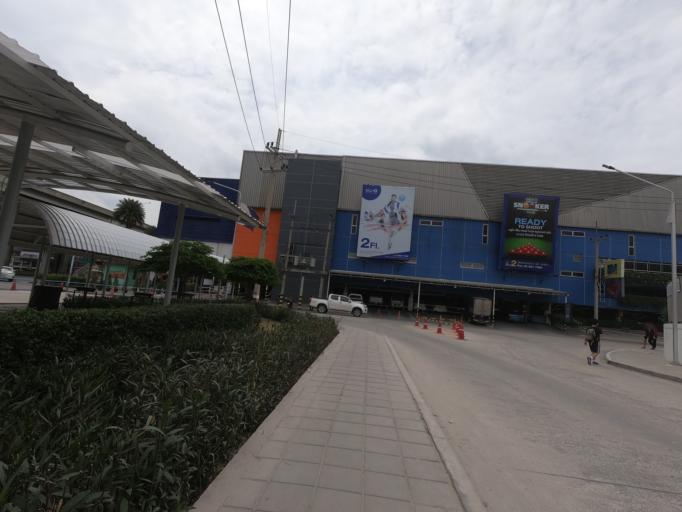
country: TH
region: Bangkok
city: Sai Mai
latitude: 13.9353
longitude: 100.6533
